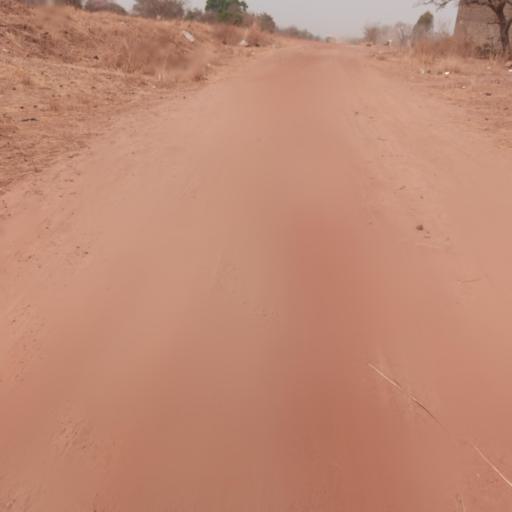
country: BF
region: Centre
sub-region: Kadiogo Province
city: Ouagadougou
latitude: 12.3427
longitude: -1.6791
